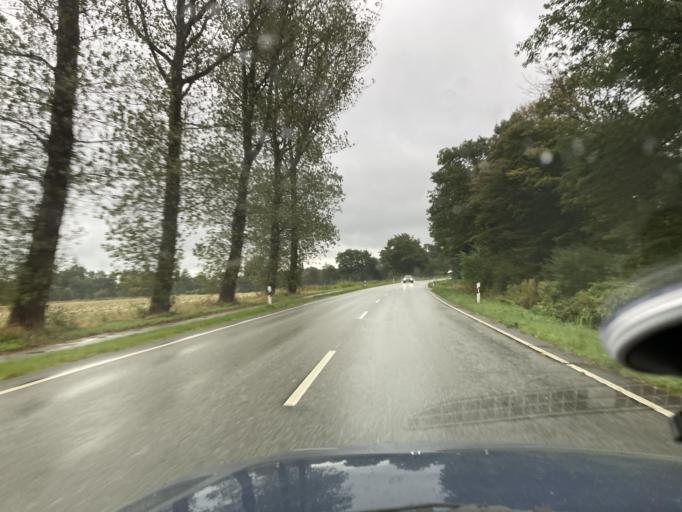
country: DE
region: Schleswig-Holstein
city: Gaushorn
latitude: 54.1963
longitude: 9.2087
